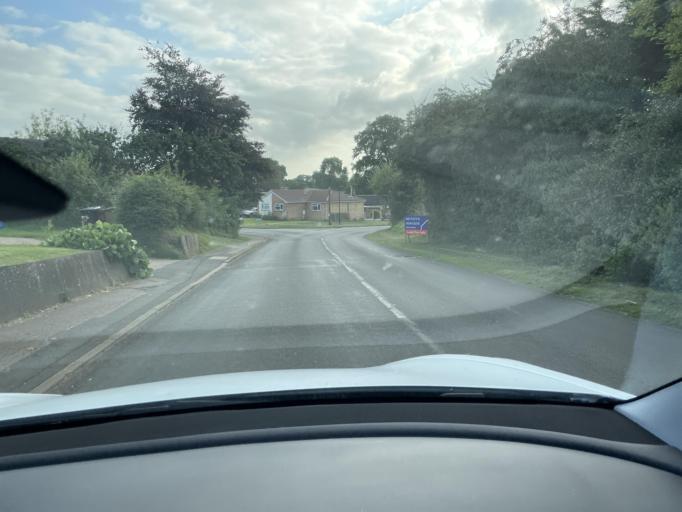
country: GB
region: England
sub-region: Leicestershire
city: Market Harborough
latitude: 52.3944
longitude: -0.9916
